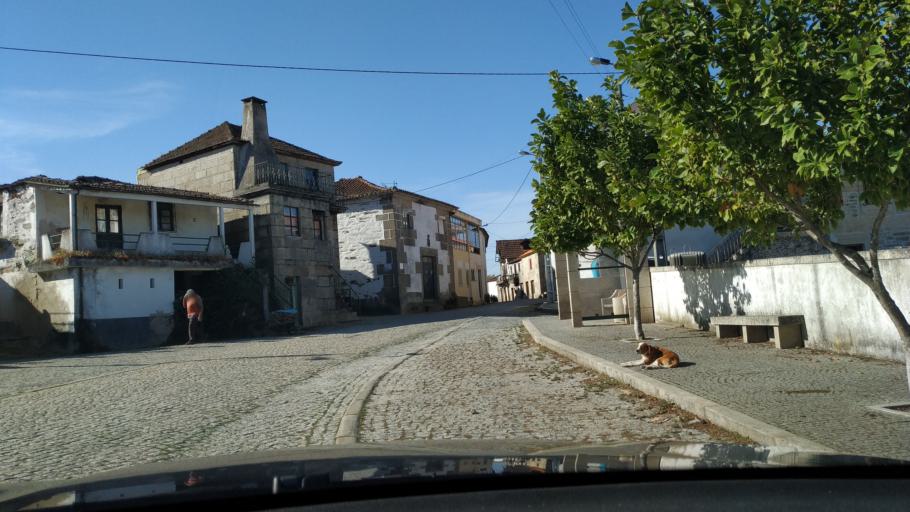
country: PT
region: Vila Real
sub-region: Sabrosa
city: Vilela
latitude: 41.2271
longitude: -7.6353
